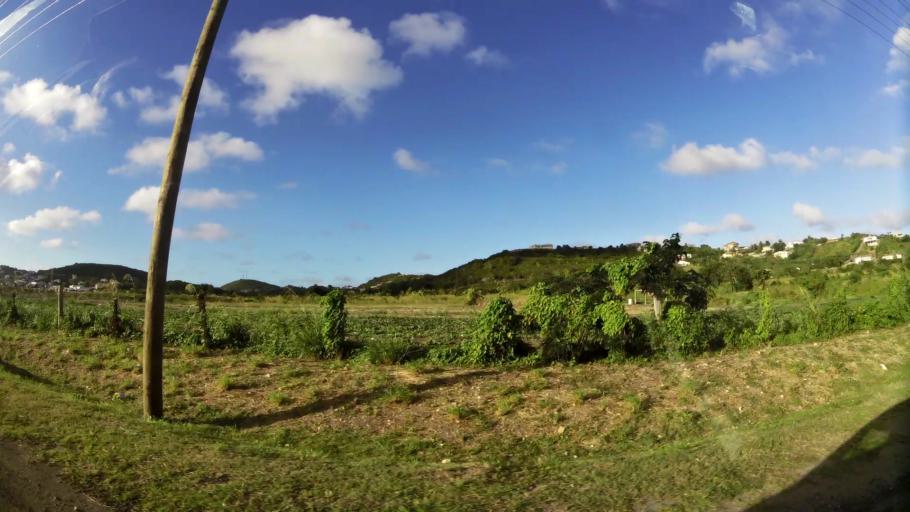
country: AG
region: Saint George
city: Piggotts
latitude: 17.1304
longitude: -61.8085
